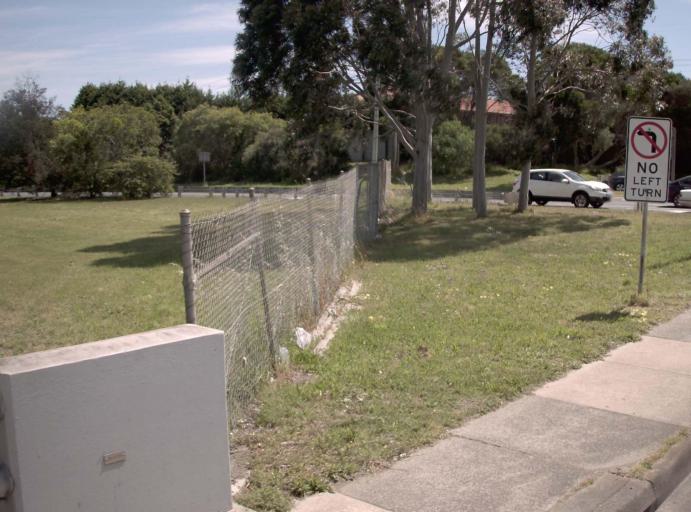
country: AU
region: Victoria
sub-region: Monash
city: Notting Hill
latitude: -37.8942
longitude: 145.1441
